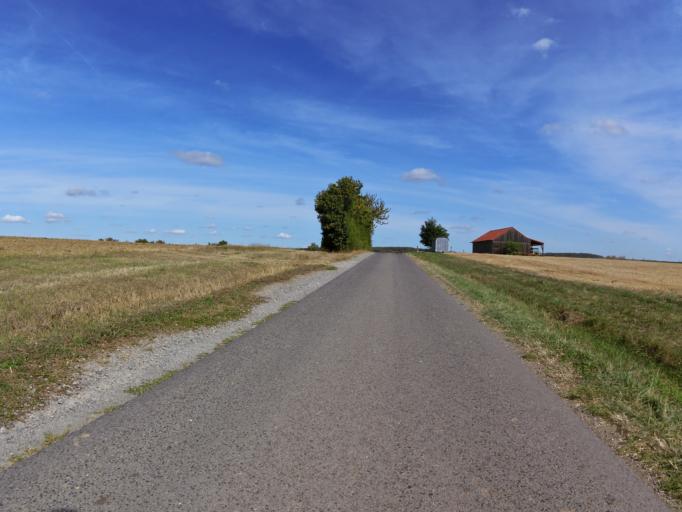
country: DE
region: Bavaria
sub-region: Regierungsbezirk Unterfranken
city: Rimpar
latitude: 49.8474
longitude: 9.9385
